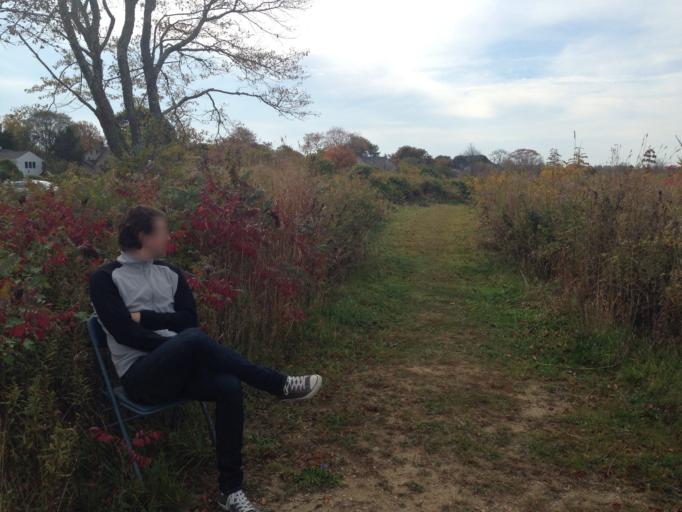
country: US
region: Connecticut
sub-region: New London County
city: Pawcatuck
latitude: 41.3299
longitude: -71.8361
